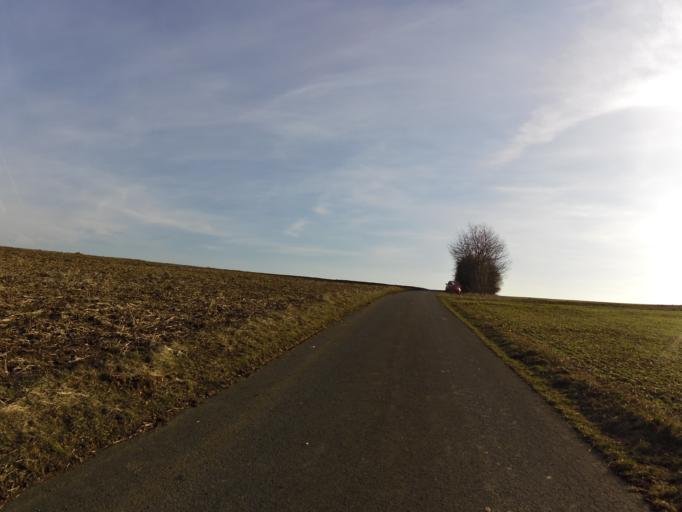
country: DE
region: Bavaria
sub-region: Regierungsbezirk Unterfranken
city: Estenfeld
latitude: 49.8355
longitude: 10.0192
